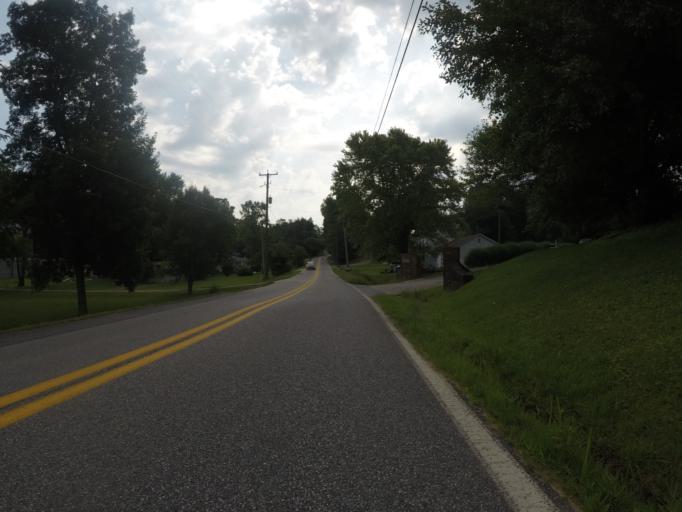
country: US
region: West Virginia
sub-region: Cabell County
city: Barboursville
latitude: 38.3814
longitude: -82.2644
